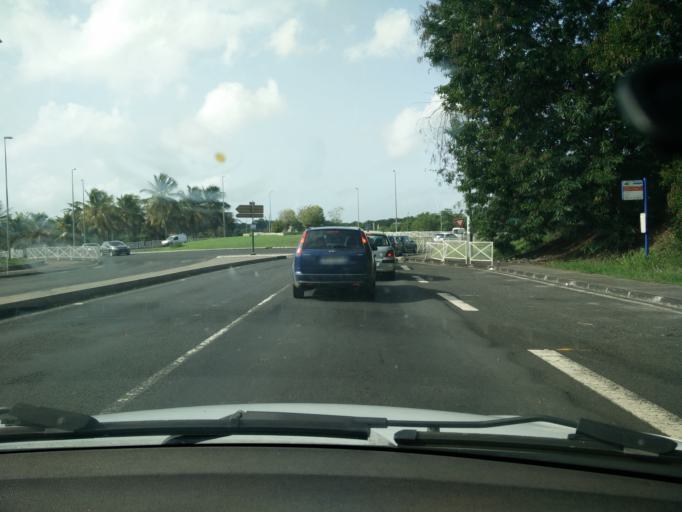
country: GP
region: Guadeloupe
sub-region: Guadeloupe
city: Baie-Mahault
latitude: 16.2555
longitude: -61.5709
